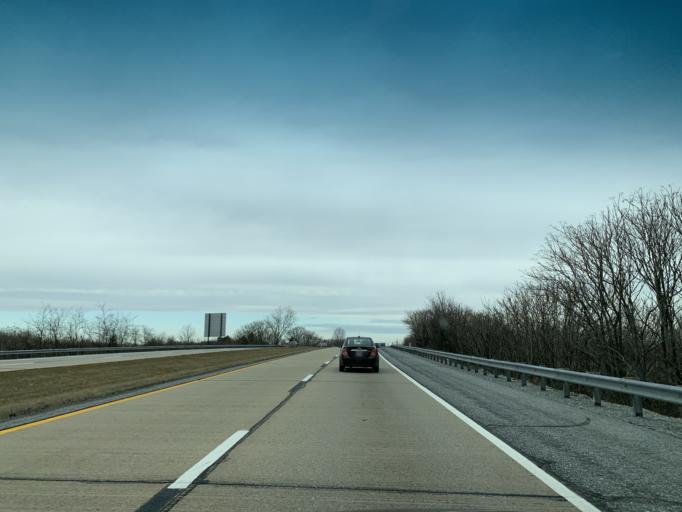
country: US
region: West Virginia
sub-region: Jefferson County
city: Ranson
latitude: 39.3245
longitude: -77.8527
